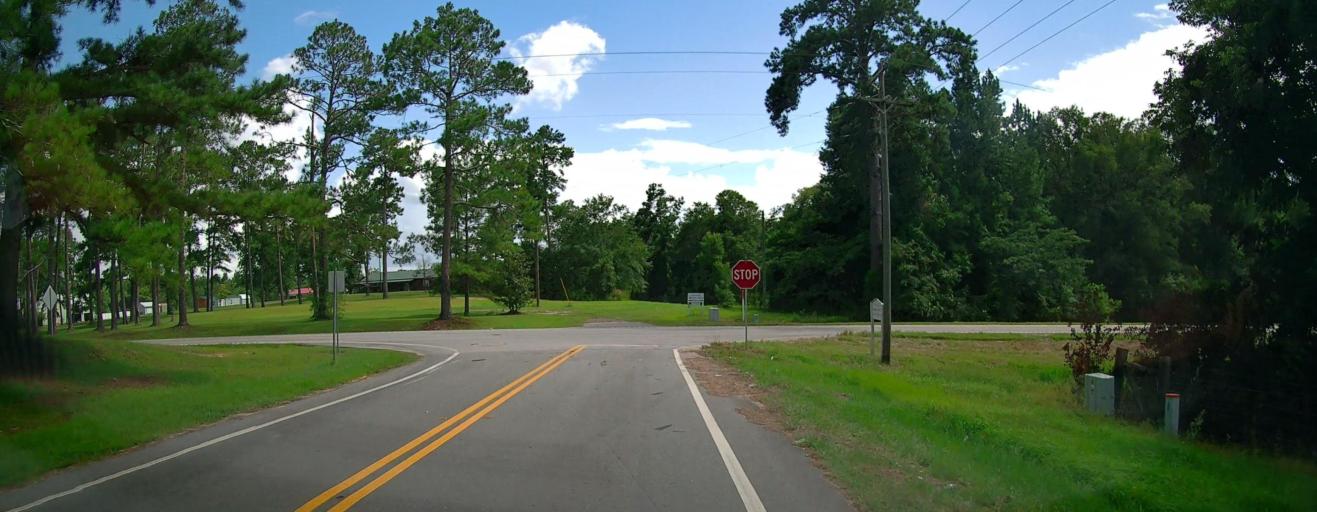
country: US
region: Georgia
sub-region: Irwin County
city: Ocilla
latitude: 31.5964
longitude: -83.1655
